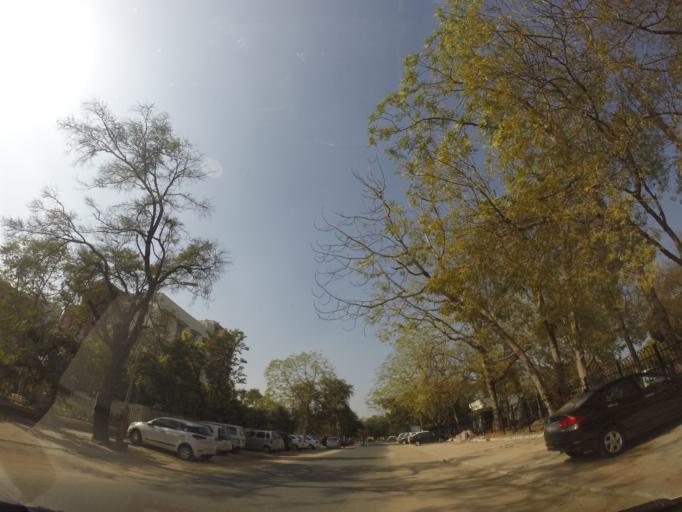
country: IN
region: Gujarat
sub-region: Gandhinagar
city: Ghandinagar
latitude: 23.2217
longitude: 72.6456
